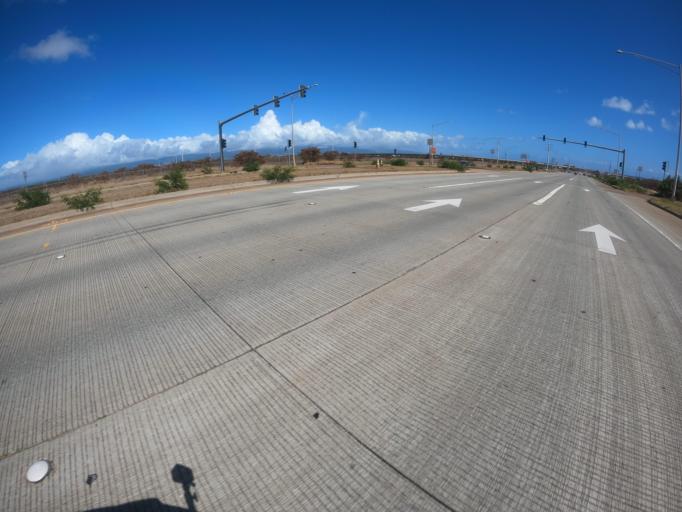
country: US
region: Hawaii
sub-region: Honolulu County
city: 'Ewa Villages
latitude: 21.3640
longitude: -158.0578
